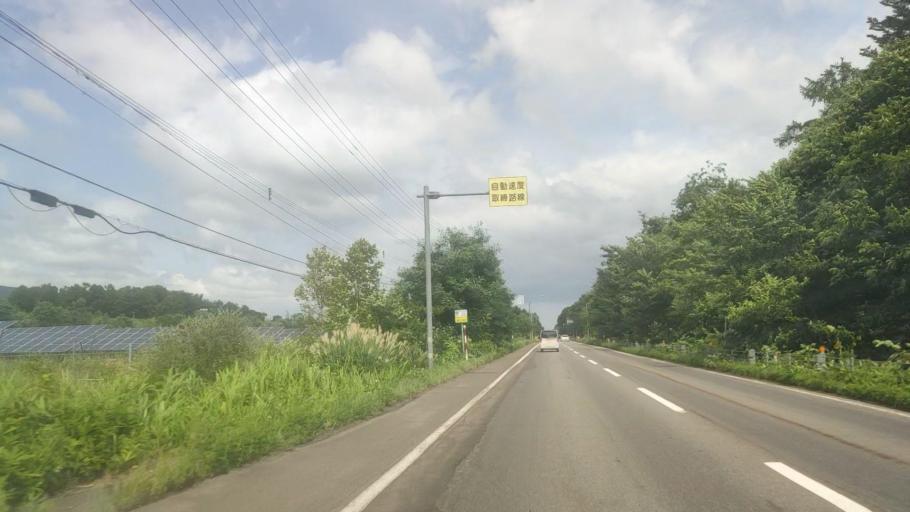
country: JP
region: Hokkaido
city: Nanae
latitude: 42.0277
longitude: 140.6114
